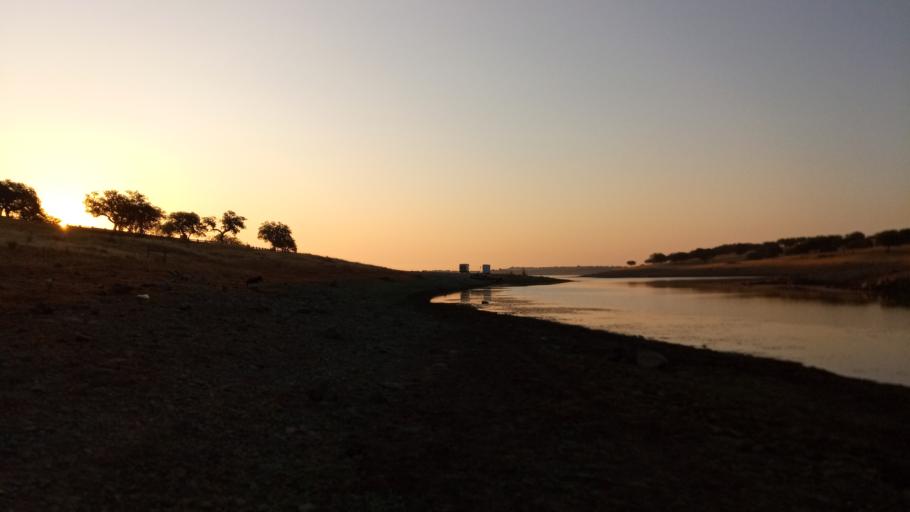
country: PT
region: Evora
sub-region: Mourao
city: Mourao
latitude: 38.3550
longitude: -7.4463
